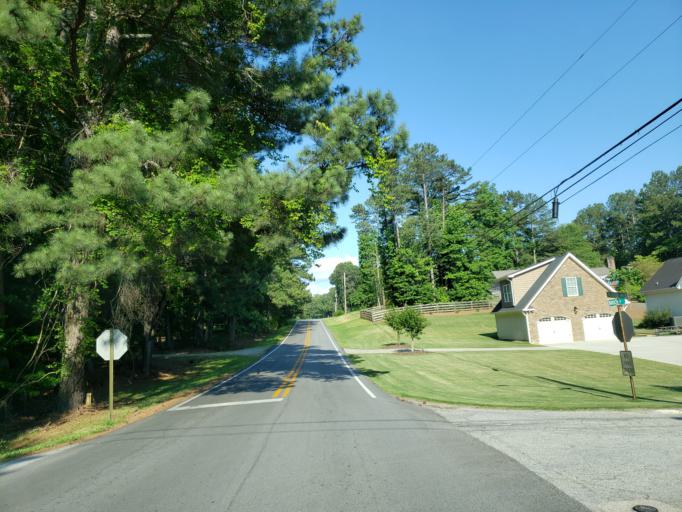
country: US
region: Georgia
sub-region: Haralson County
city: Bremen
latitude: 33.7123
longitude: -85.1245
